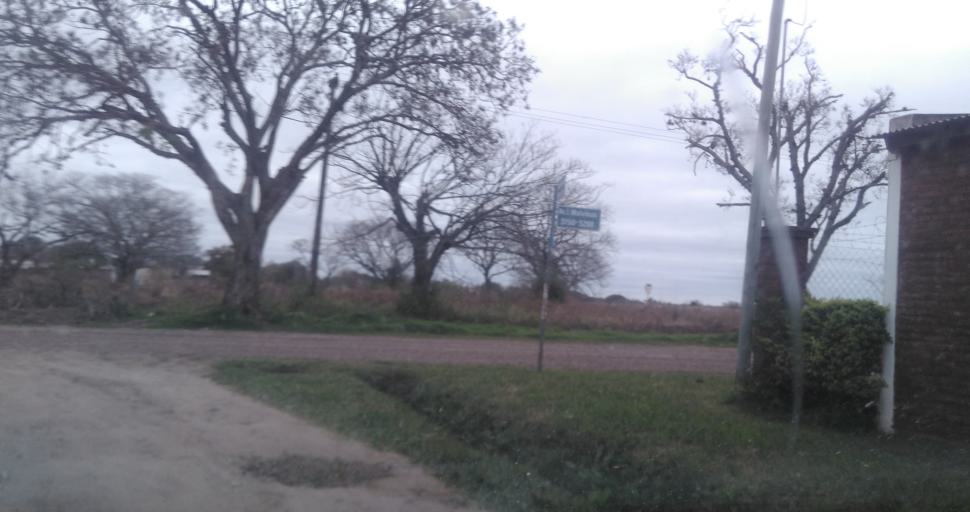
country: AR
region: Chaco
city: Fontana
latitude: -27.4448
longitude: -59.0363
